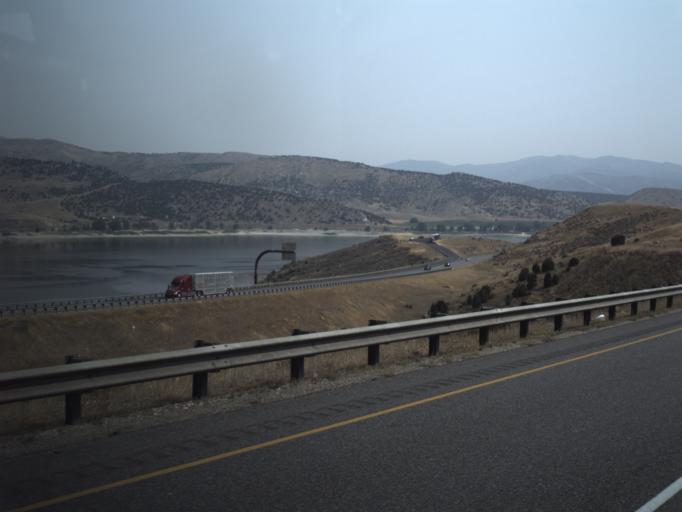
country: US
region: Utah
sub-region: Summit County
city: Coalville
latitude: 40.9496
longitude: -111.4212
